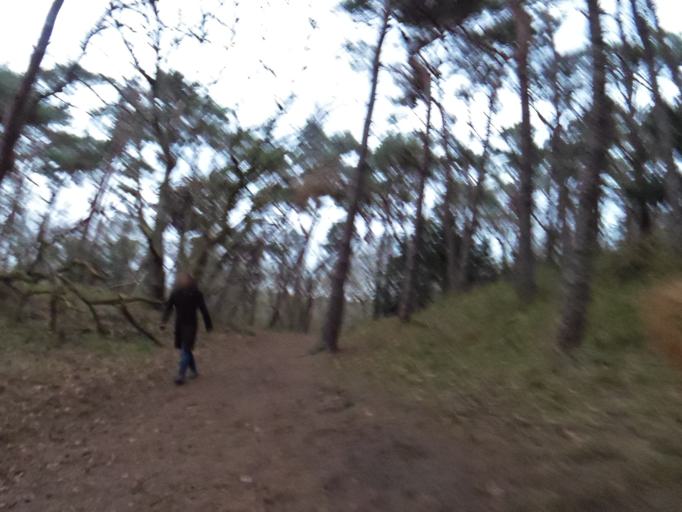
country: NL
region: North Holland
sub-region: Gemeente Bloemendaal
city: Bennebroek
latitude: 52.3558
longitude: 4.5735
